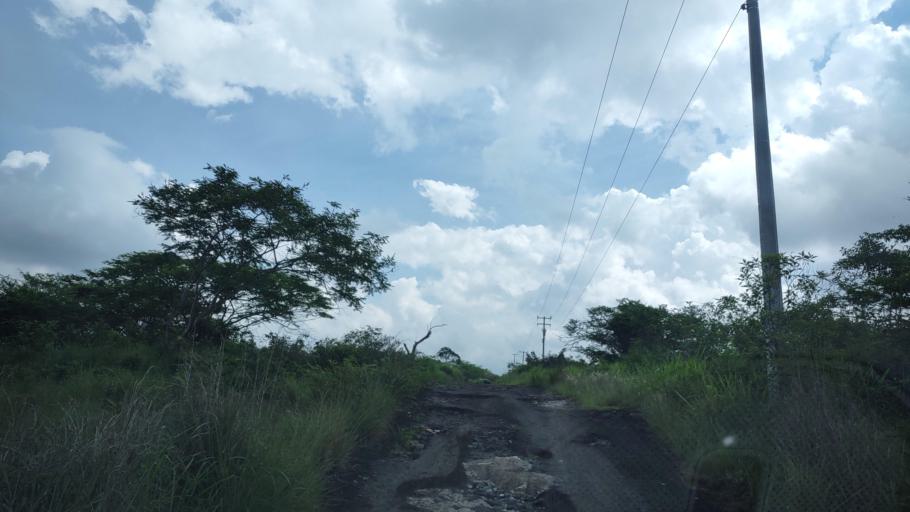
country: MX
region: Veracruz
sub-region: Emiliano Zapata
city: Dos Rios
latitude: 19.4537
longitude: -96.8088
